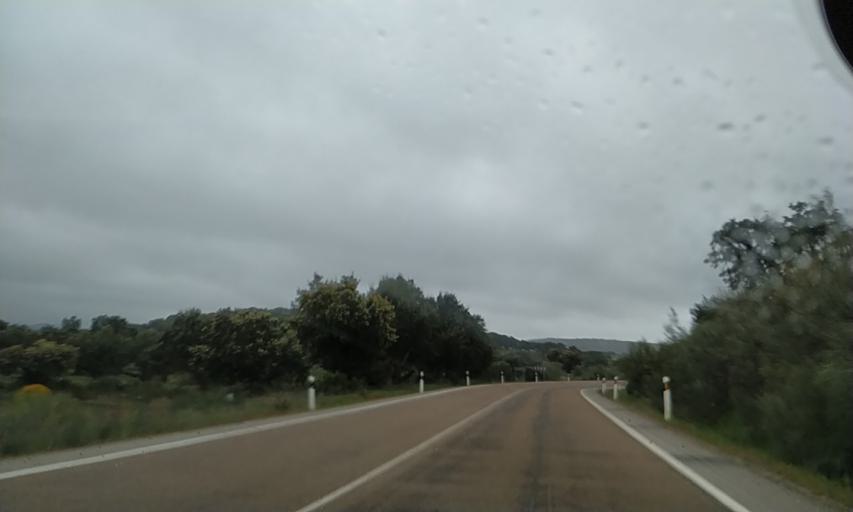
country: ES
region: Extremadura
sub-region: Provincia de Badajoz
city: Puebla de Obando
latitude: 39.2741
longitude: -6.5205
